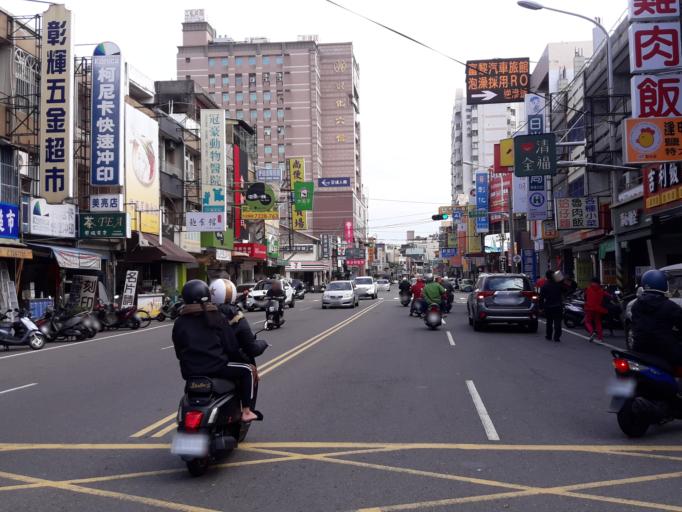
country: TW
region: Taiwan
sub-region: Changhua
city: Chang-hua
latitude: 24.0897
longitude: 120.5367
